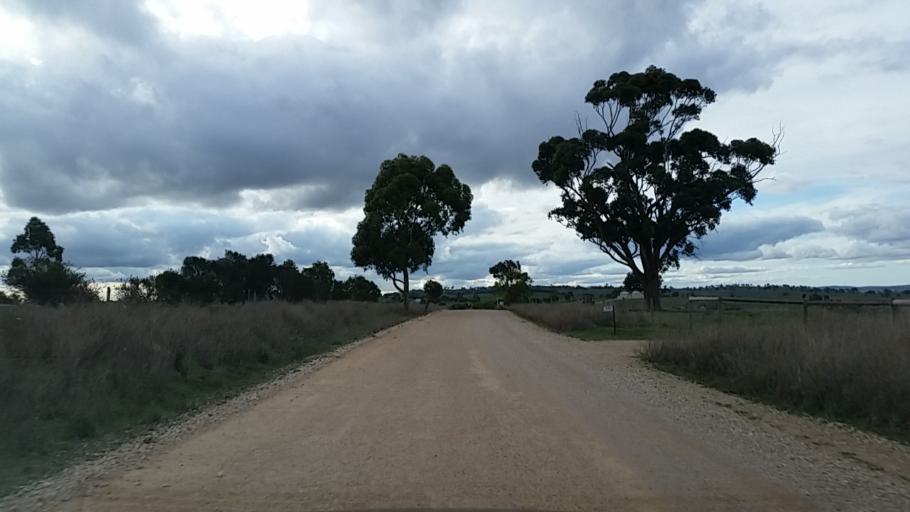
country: AU
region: South Australia
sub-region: Mount Barker
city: Callington
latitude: -34.9843
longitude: 139.0577
